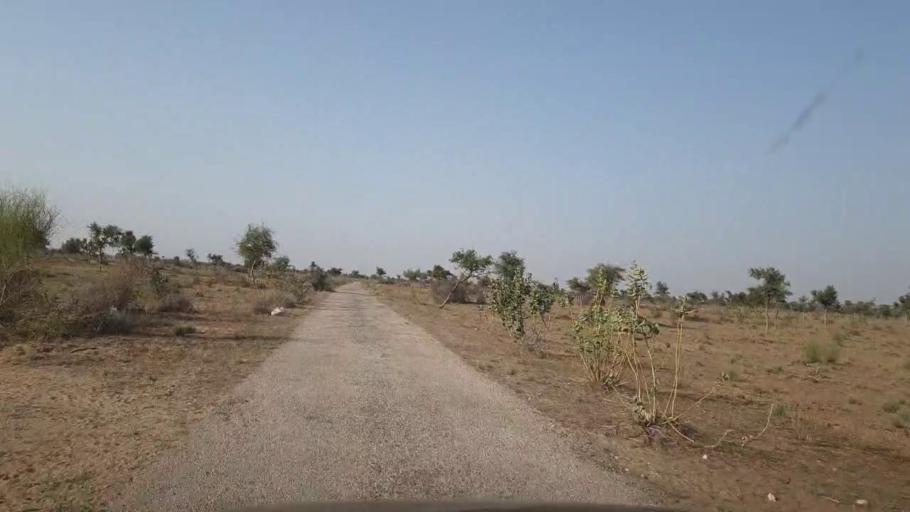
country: PK
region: Sindh
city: Islamkot
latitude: 25.1067
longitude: 70.4158
